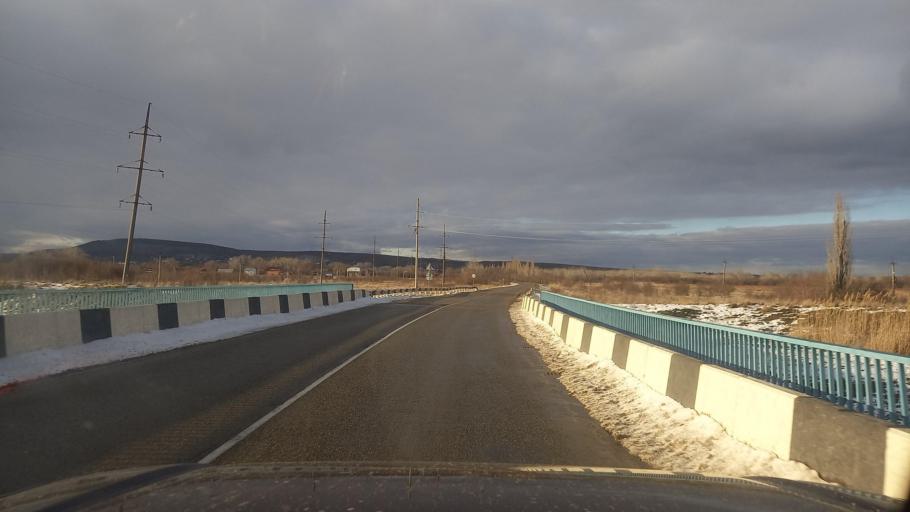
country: RU
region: Krasnodarskiy
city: Smolenskaya
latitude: 44.7729
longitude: 38.8172
